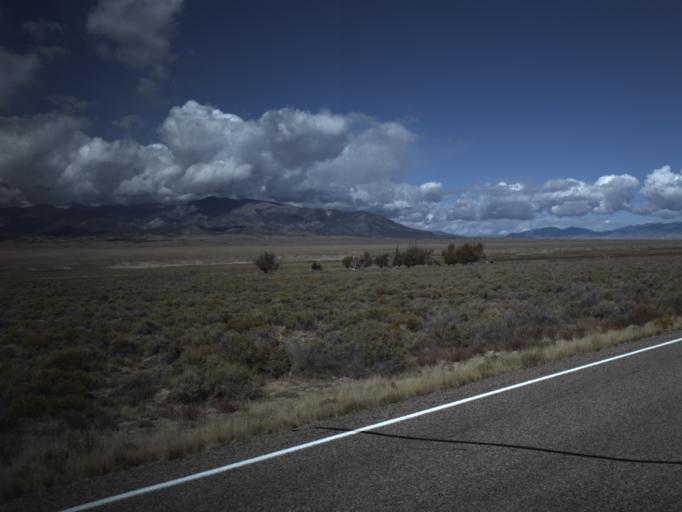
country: US
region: Nevada
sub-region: White Pine County
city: McGill
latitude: 38.8270
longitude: -113.9881
